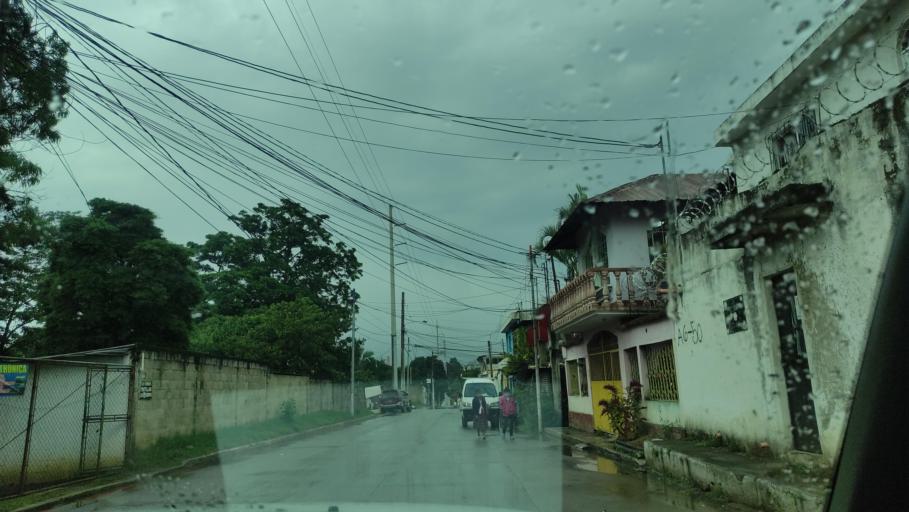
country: GT
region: Guatemala
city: Petapa
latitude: 14.5002
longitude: -90.5569
